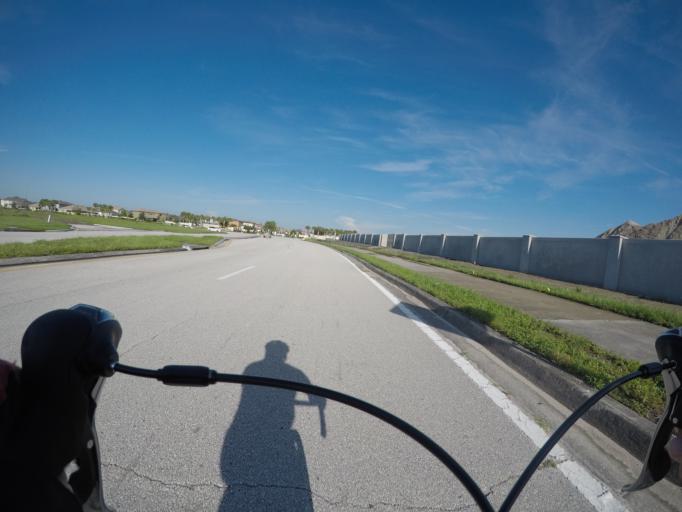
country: US
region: Florida
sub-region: Osceola County
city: Buenaventura Lakes
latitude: 28.3656
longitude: -81.3242
